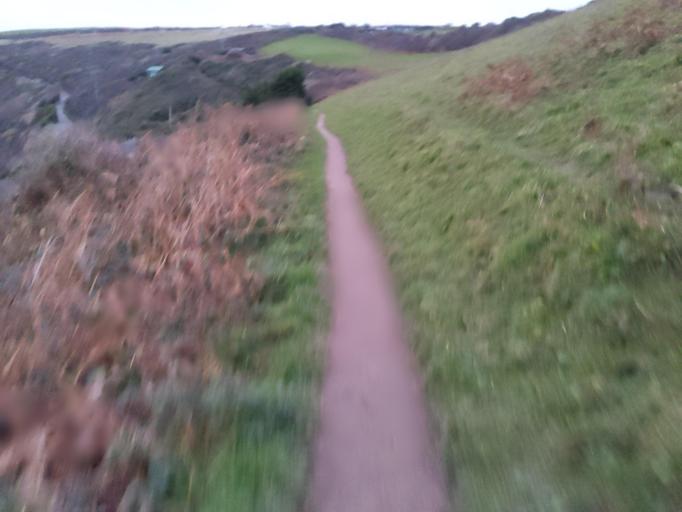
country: GB
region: England
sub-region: Cornwall
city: Millbrook
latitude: 50.3211
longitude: -4.2198
